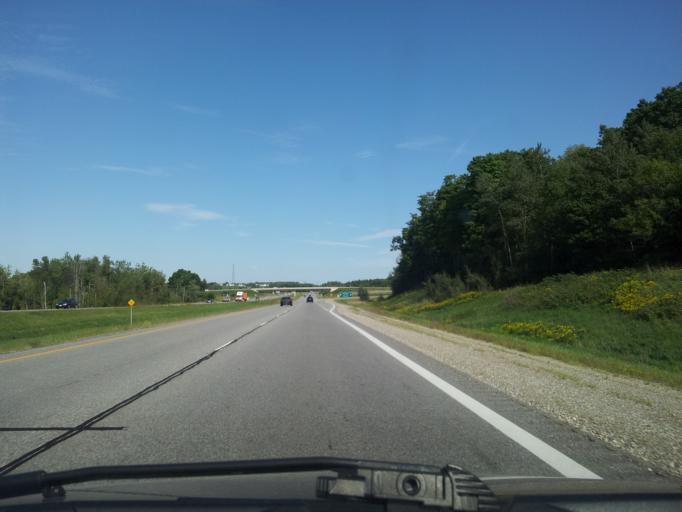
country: CA
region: Ontario
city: Kitchener
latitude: 43.4037
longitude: -80.6050
